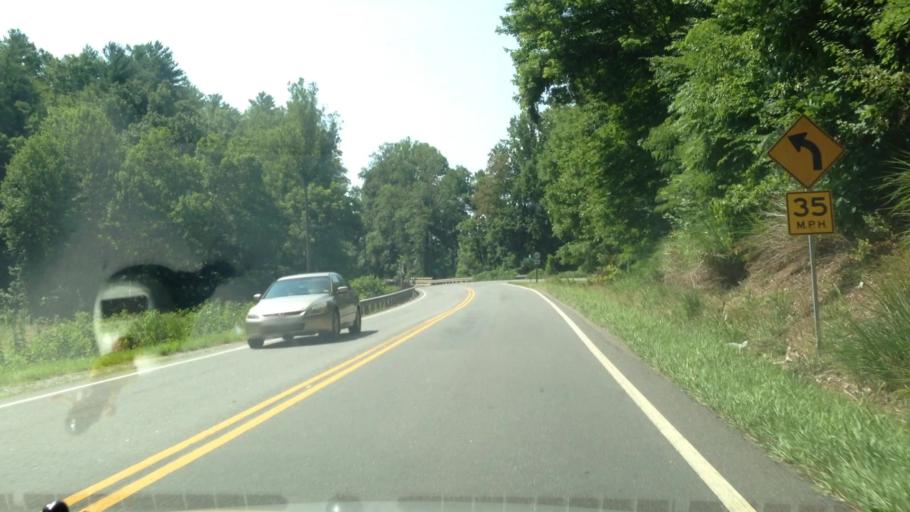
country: US
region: Virginia
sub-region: Patrick County
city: Stuart
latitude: 36.5794
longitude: -80.3810
